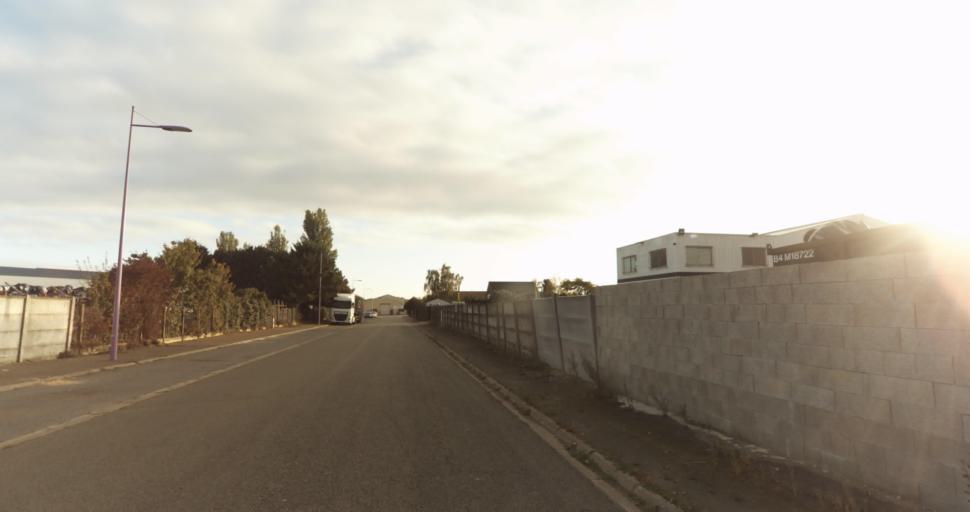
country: FR
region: Centre
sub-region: Departement d'Eure-et-Loir
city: Vernouillet
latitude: 48.7131
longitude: 1.3764
